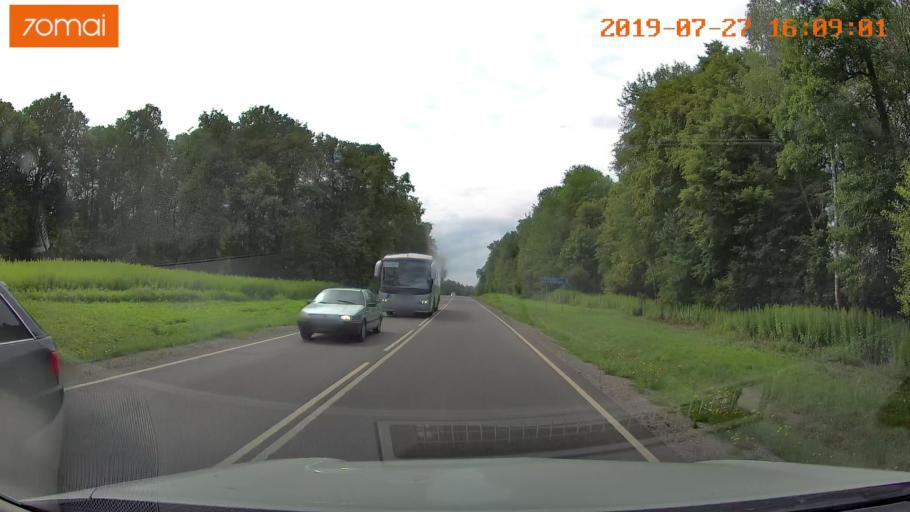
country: RU
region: Kaliningrad
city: Chernyakhovsk
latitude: 54.6384
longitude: 21.7237
